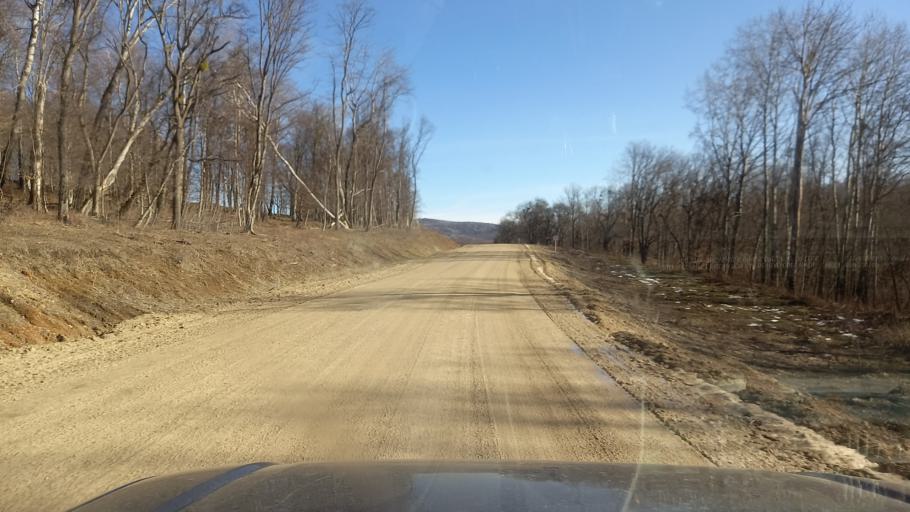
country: RU
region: Adygeya
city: Kamennomostskiy
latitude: 44.2823
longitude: 40.3163
